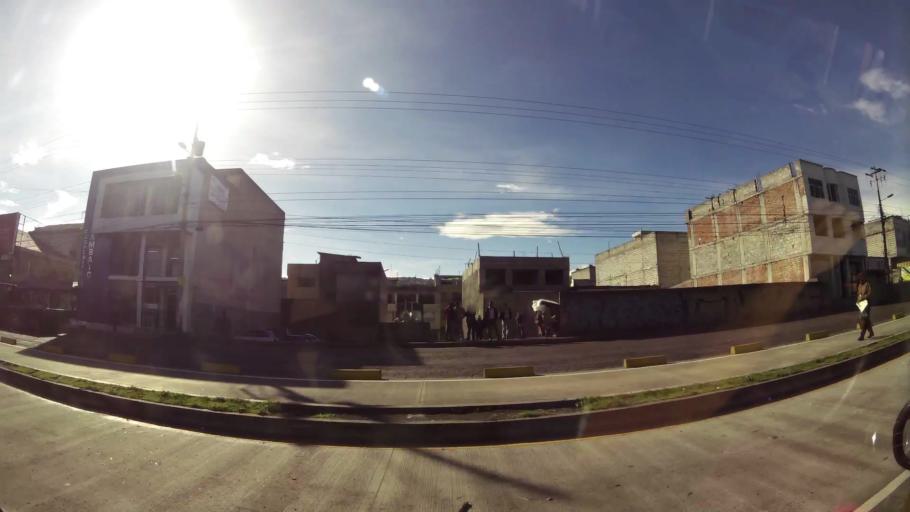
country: EC
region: Pichincha
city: Quito
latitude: -0.3046
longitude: -78.5430
